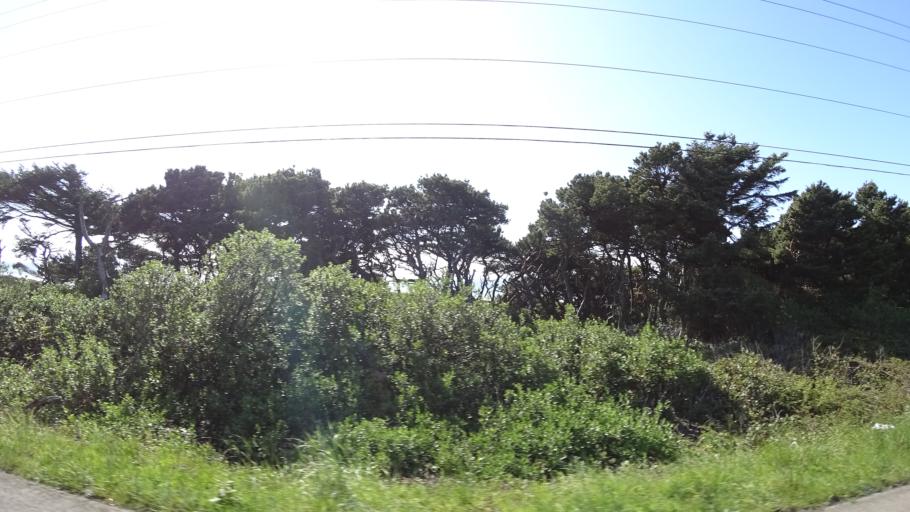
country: US
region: Oregon
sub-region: Lincoln County
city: Newport
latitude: 44.5556
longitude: -124.0716
